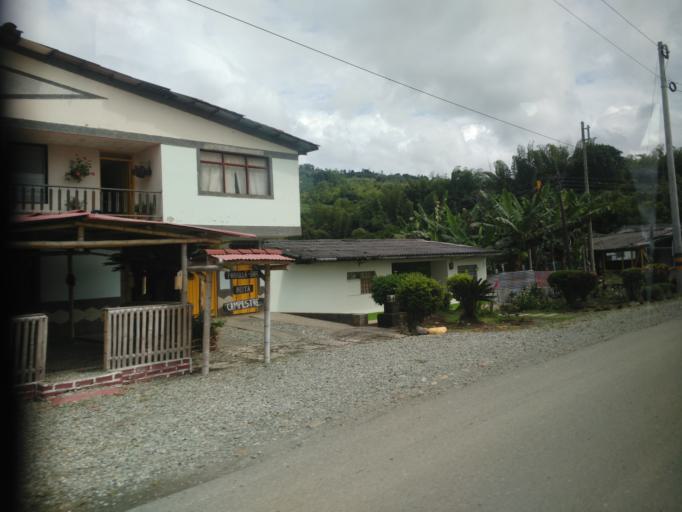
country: CO
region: Valle del Cauca
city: Caicedonia
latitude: 4.3194
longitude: -75.8743
